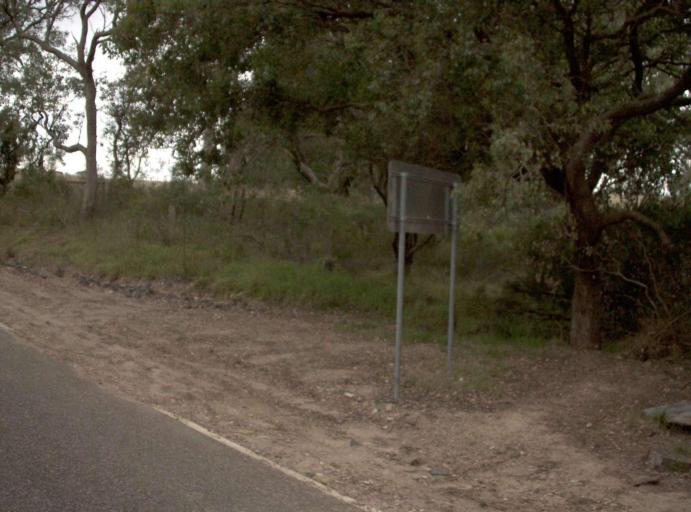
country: AU
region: Victoria
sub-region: Wellington
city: Sale
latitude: -38.0124
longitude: 147.1889
